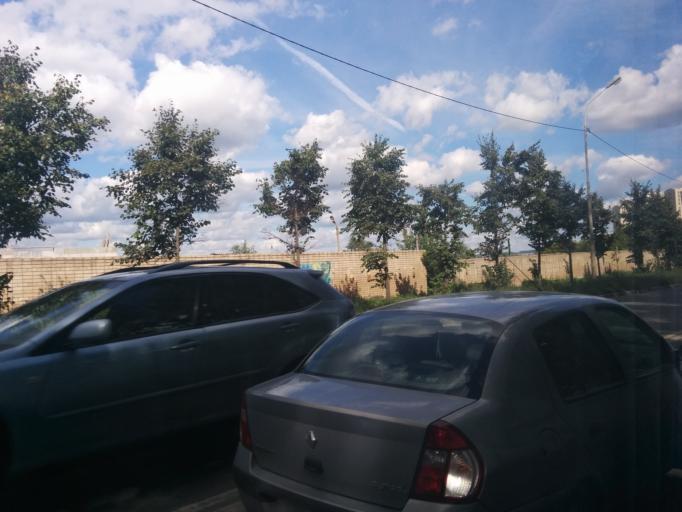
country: RU
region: Tatarstan
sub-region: Gorod Kazan'
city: Kazan
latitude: 55.7955
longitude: 49.1978
